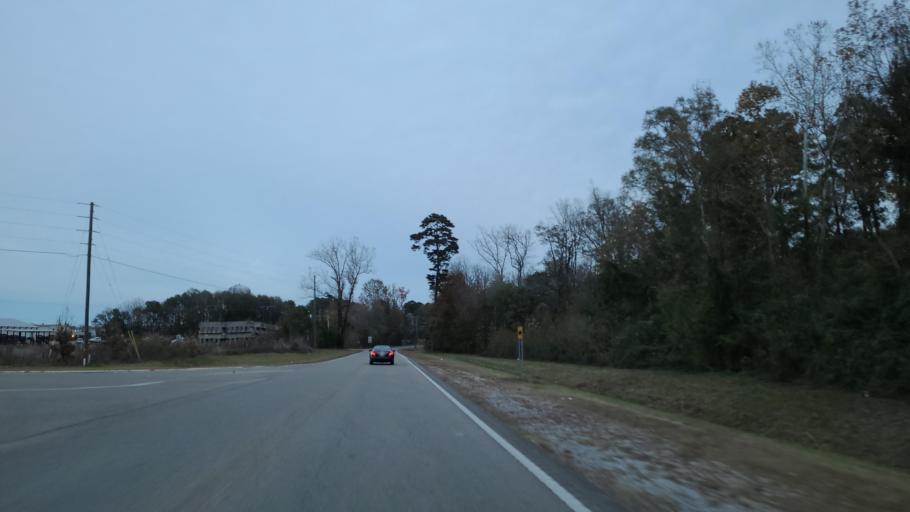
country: US
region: Mississippi
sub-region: Clarke County
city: Quitman
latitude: 32.0420
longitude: -88.7394
